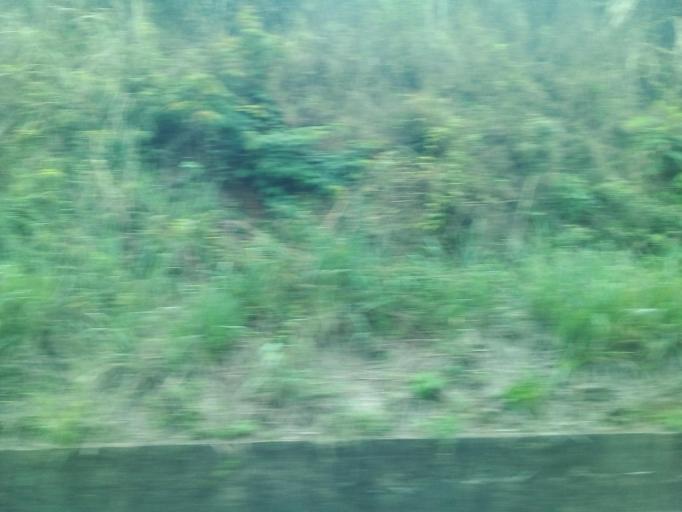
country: BR
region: Minas Gerais
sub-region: Nova Era
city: Nova Era
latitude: -19.7314
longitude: -42.9982
